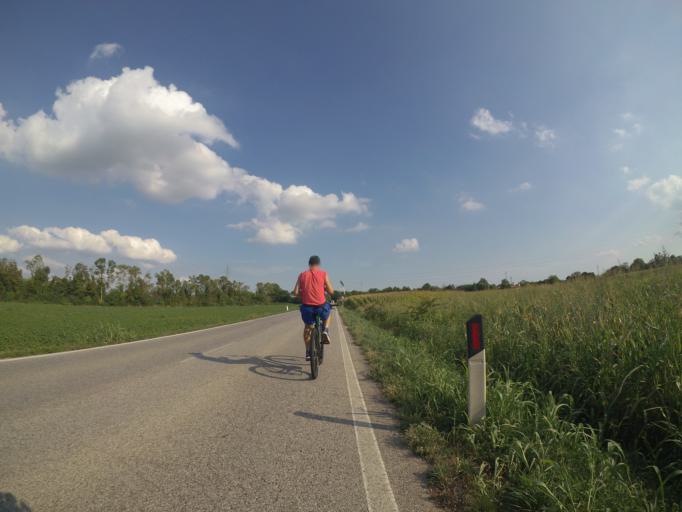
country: IT
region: Friuli Venezia Giulia
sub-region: Provincia di Udine
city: Basiliano-Vissandone
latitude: 46.0446
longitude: 13.0963
